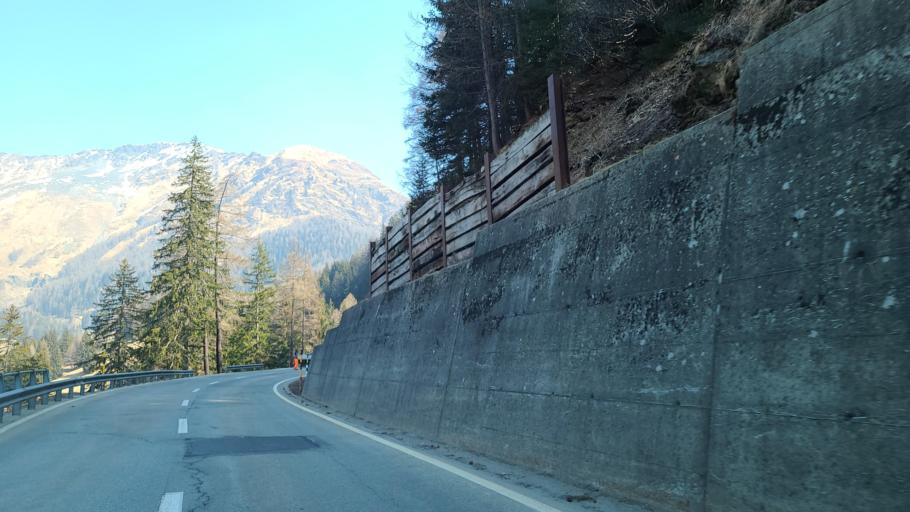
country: CH
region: Grisons
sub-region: Bernina District
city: Poschiavo
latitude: 46.3787
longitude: 10.0712
